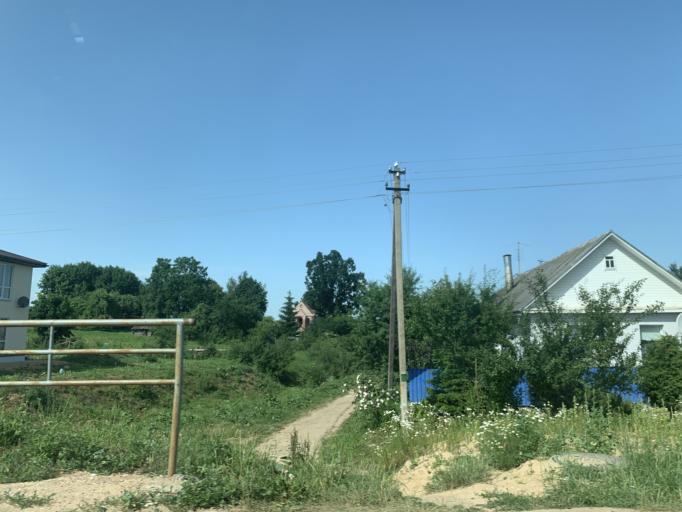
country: BY
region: Minsk
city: Dzyarzhynsk
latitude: 53.6964
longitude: 27.1079
